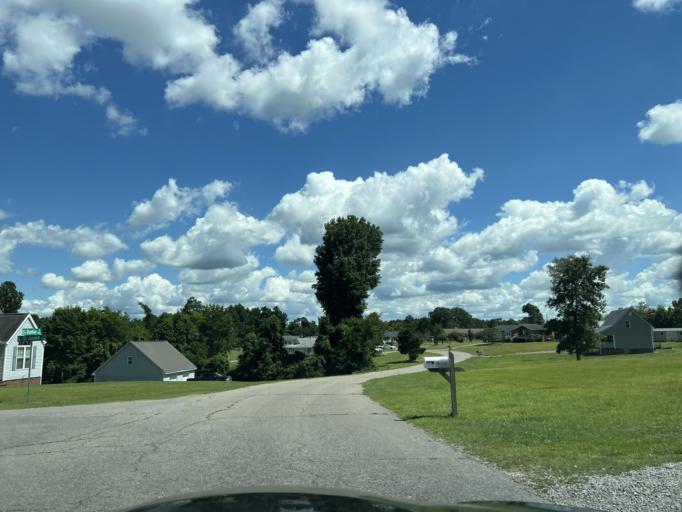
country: US
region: North Carolina
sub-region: Lee County
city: Sanford
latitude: 35.4330
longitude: -79.1609
